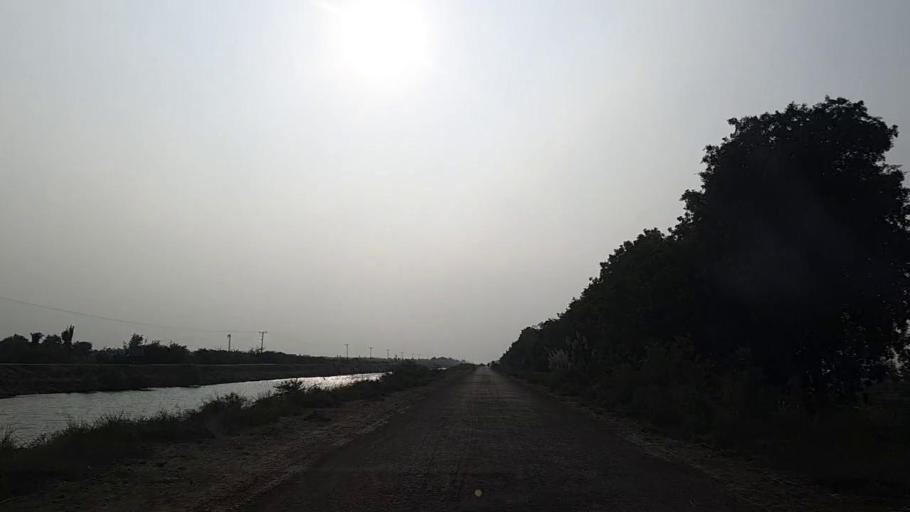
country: PK
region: Sindh
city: Mirpur Sakro
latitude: 24.6314
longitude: 67.5780
